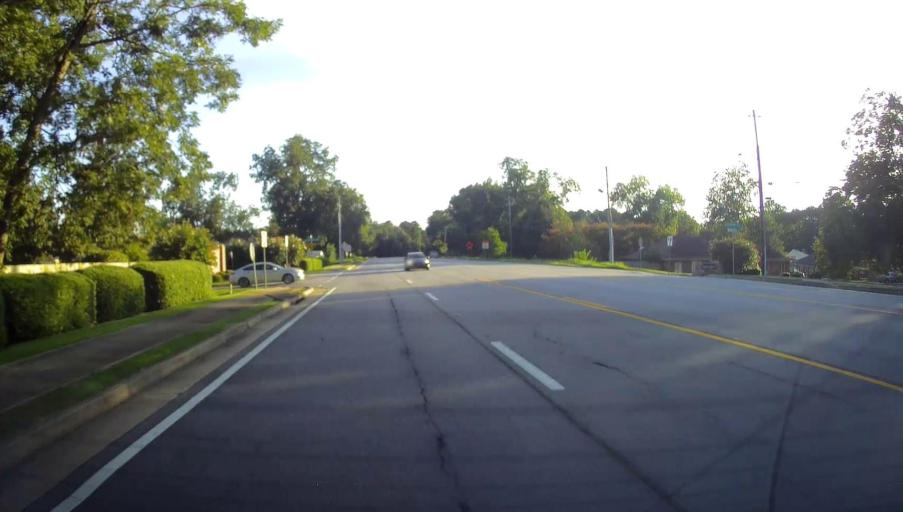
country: US
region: Georgia
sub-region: Muscogee County
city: Columbus
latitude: 32.5049
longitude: -84.8973
